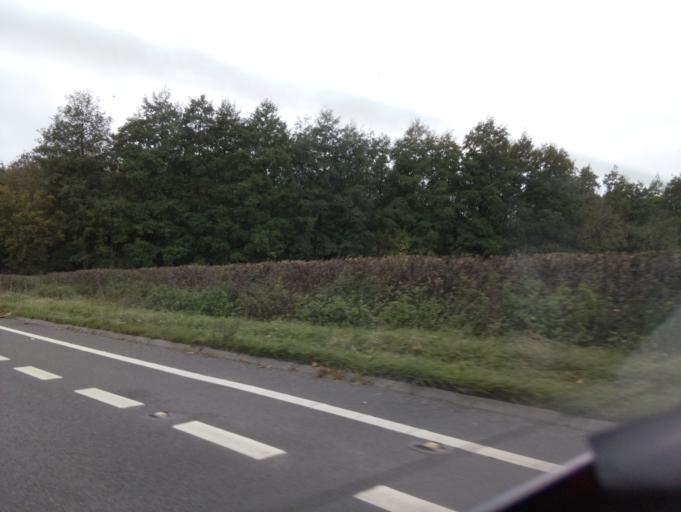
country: GB
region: England
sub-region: Somerset
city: Stoke-sub-Hamdon
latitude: 50.9616
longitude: -2.7528
